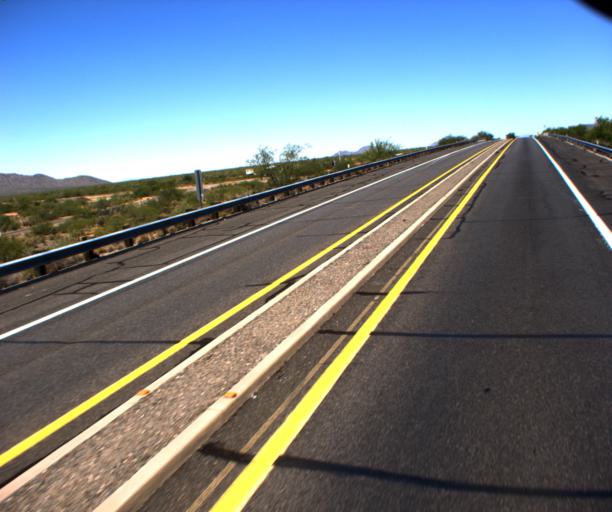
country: US
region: Arizona
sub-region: Yavapai County
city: Congress
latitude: 34.1225
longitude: -112.9491
